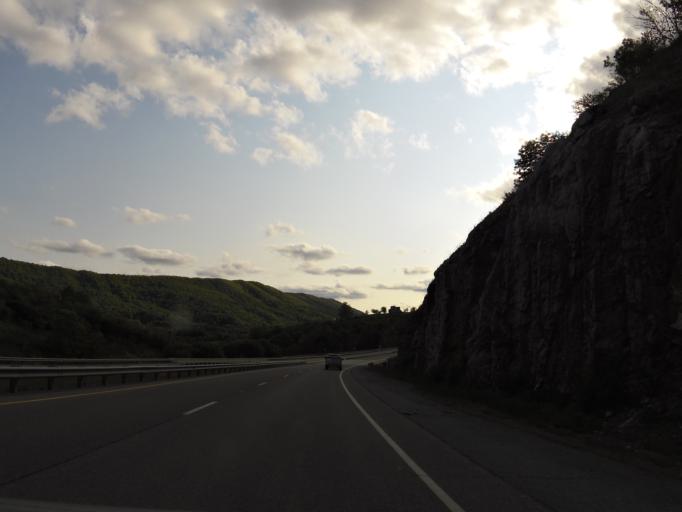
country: US
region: Virginia
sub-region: Tazewell County
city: Bluefield
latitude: 37.2354
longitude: -81.2842
